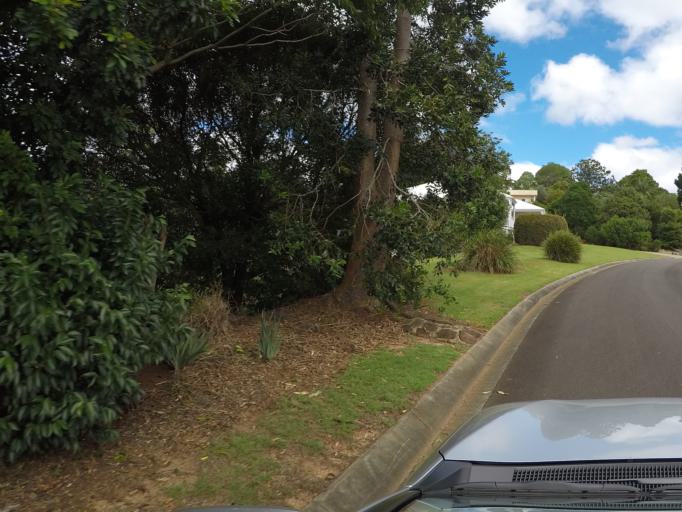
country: AU
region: Queensland
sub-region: Sunshine Coast
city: Nambour
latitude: -26.6303
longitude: 152.8710
